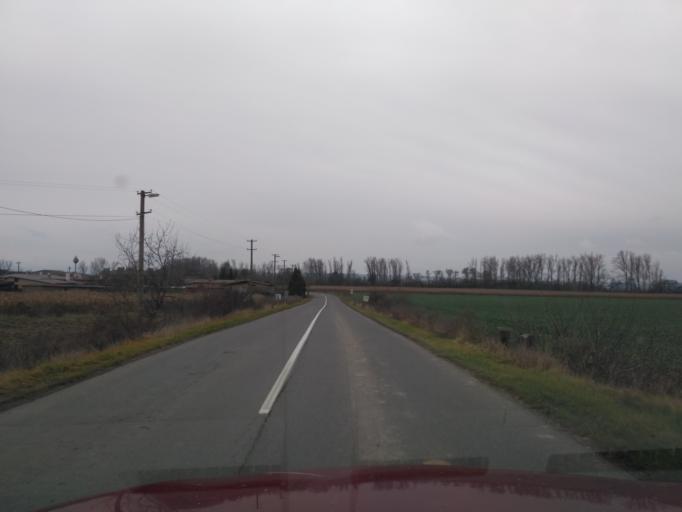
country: SK
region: Kosicky
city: Kosice
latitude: 48.5888
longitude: 21.1677
